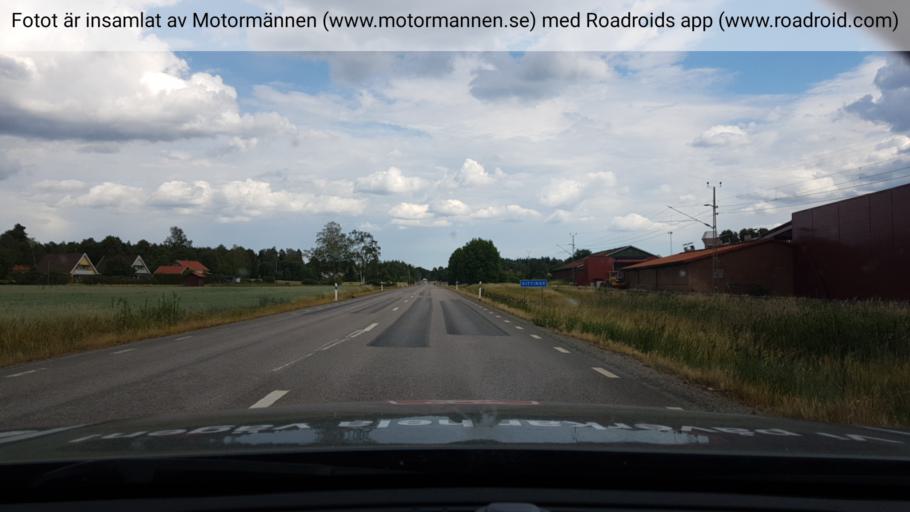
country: SE
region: Uppsala
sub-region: Heby Kommun
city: Morgongava
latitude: 59.9068
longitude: 17.0463
